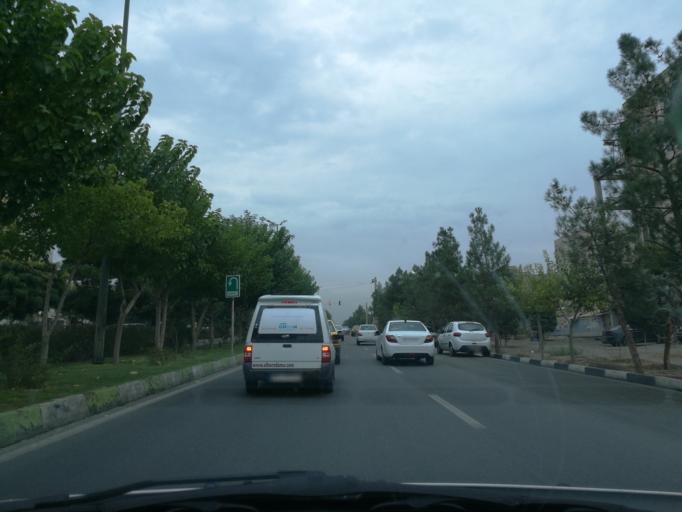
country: IR
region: Alborz
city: Karaj
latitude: 35.8605
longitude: 50.9408
